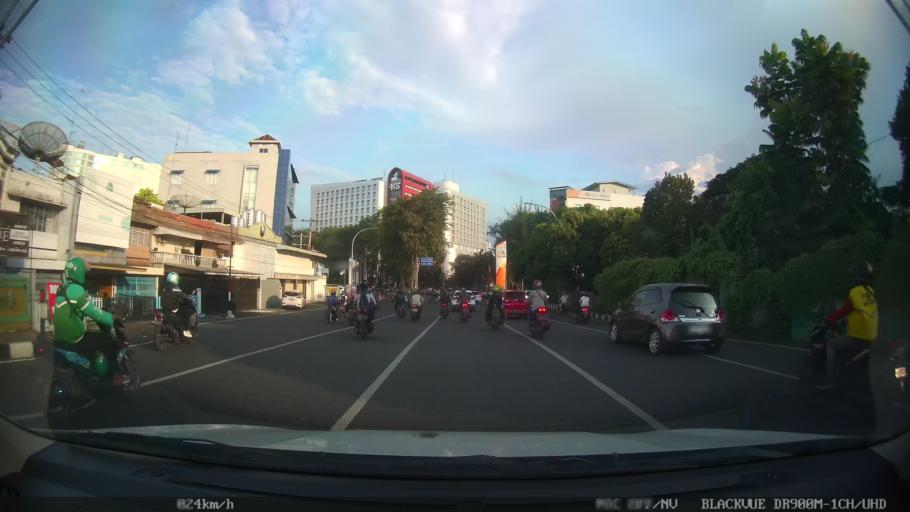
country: ID
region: North Sumatra
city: Medan
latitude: 3.5907
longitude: 98.6716
